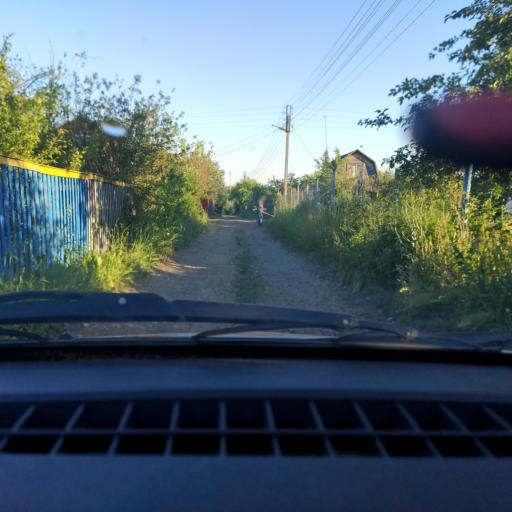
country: RU
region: Bashkortostan
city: Karmaskaly
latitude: 54.3692
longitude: 55.9032
